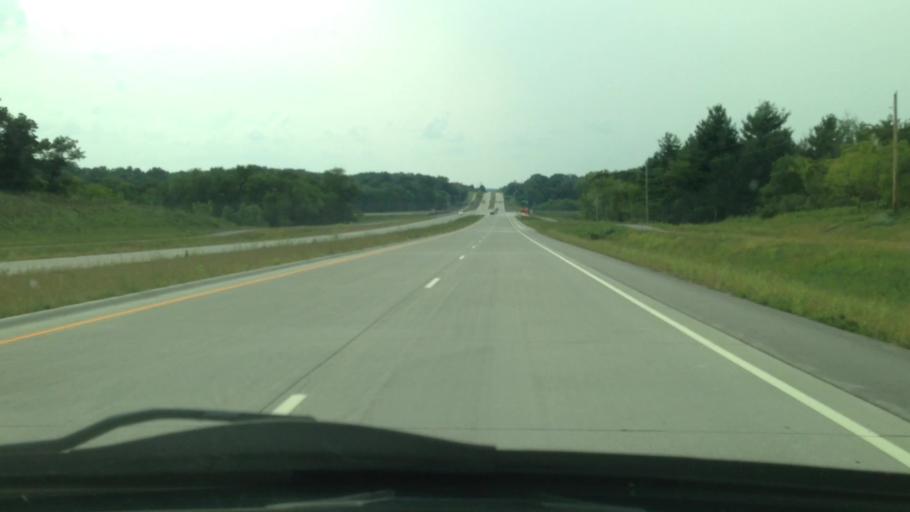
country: US
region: Minnesota
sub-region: Olmsted County
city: Rochester
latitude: 44.0795
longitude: -92.4655
